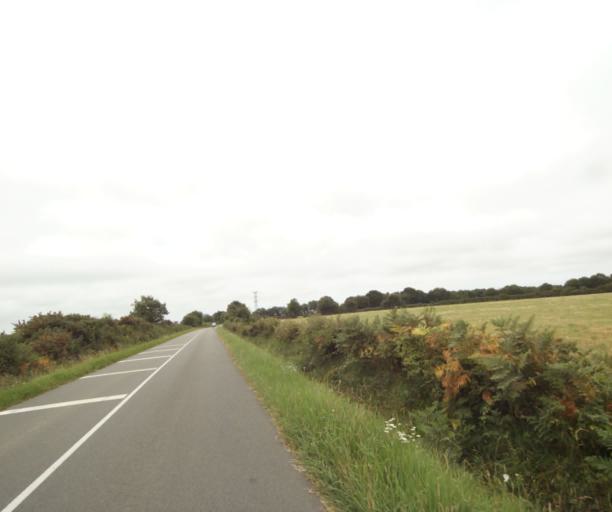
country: FR
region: Pays de la Loire
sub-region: Departement de la Vendee
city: Sainte-Foy
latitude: 46.5138
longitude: -1.6863
